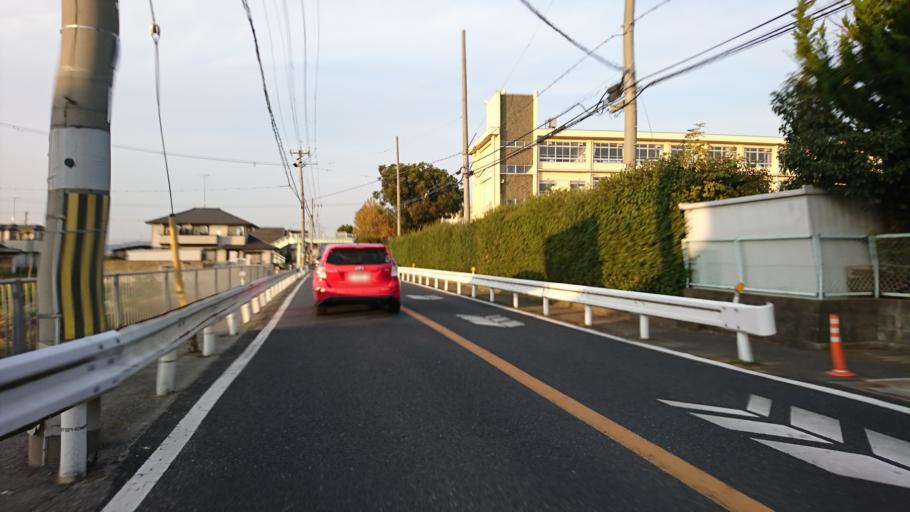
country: JP
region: Hyogo
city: Kakogawacho-honmachi
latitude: 34.7756
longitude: 134.8766
